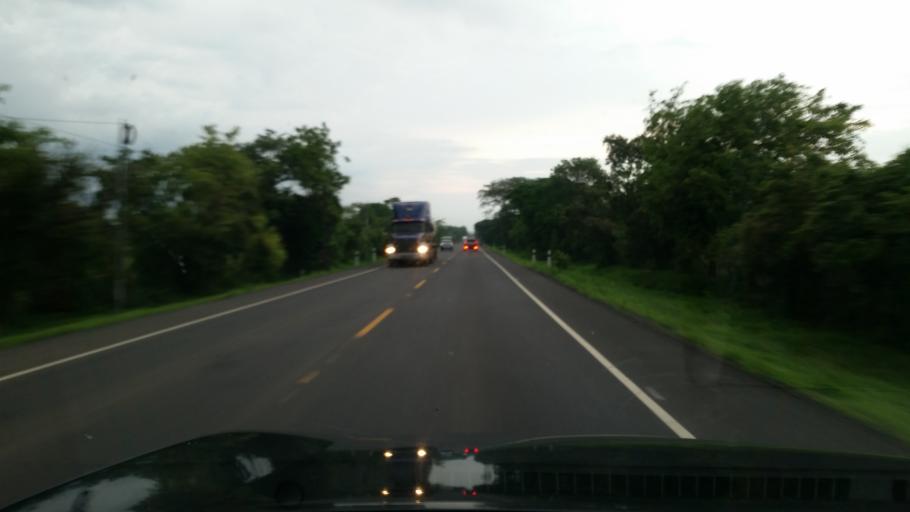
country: NI
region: Leon
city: Nagarote
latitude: 12.2925
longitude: -86.5894
